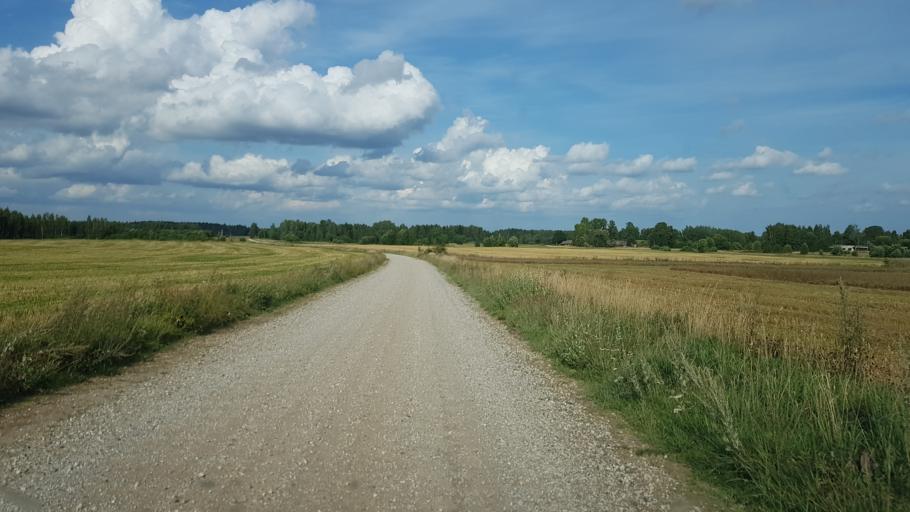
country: RU
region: Pskov
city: Pechory
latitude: 57.8006
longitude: 27.5043
